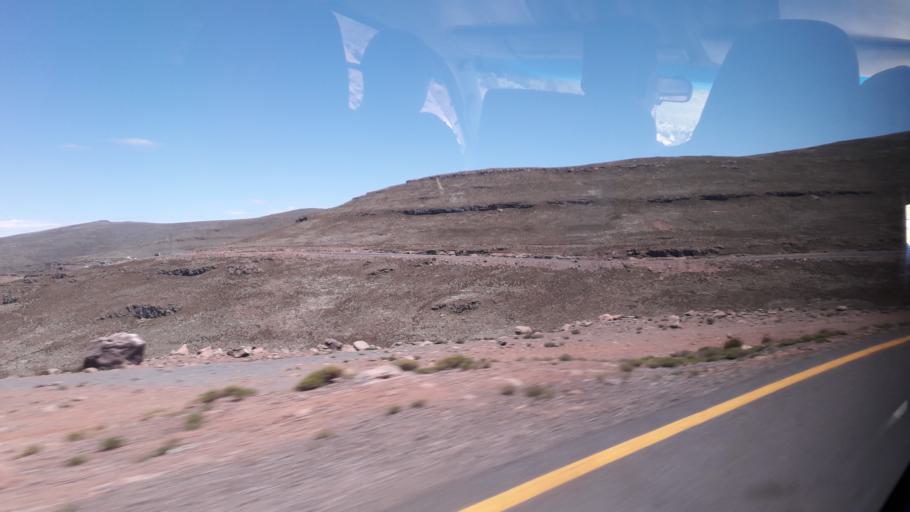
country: ZA
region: Orange Free State
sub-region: Thabo Mofutsanyana District Municipality
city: Phuthaditjhaba
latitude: -28.8330
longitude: 28.7402
